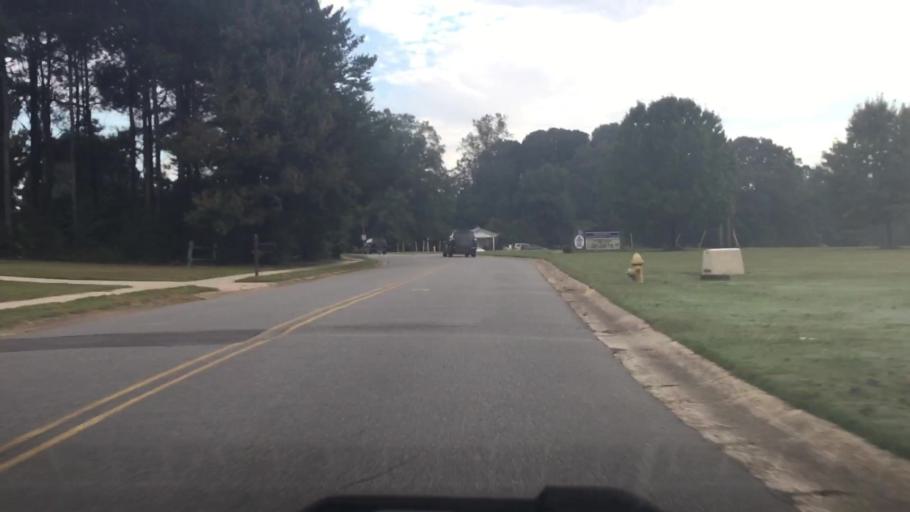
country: US
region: North Carolina
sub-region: Iredell County
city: Mooresville
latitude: 35.5641
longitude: -80.8006
